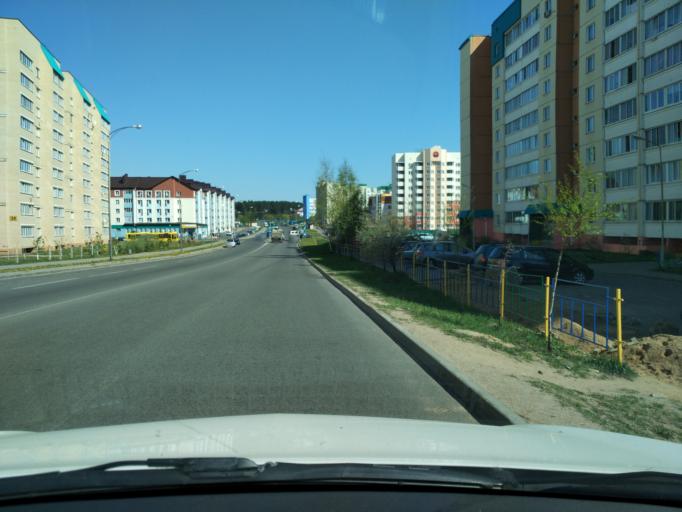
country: BY
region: Minsk
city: Borovlyany
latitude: 53.9993
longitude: 27.6802
